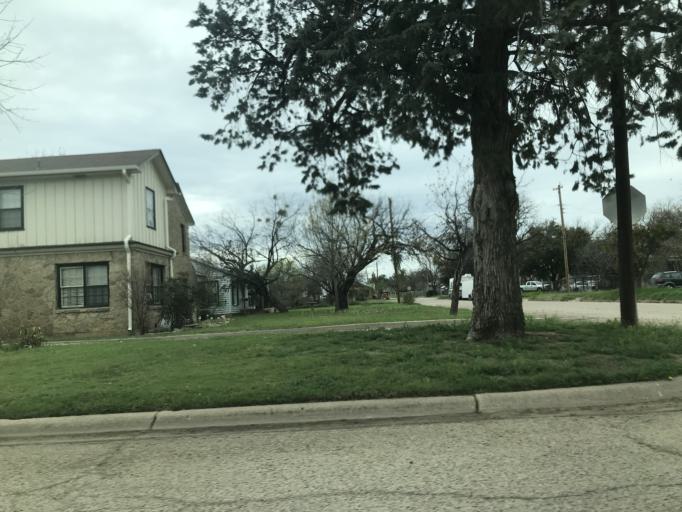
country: US
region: Texas
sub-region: Taylor County
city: Abilene
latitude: 32.4650
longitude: -99.7377
